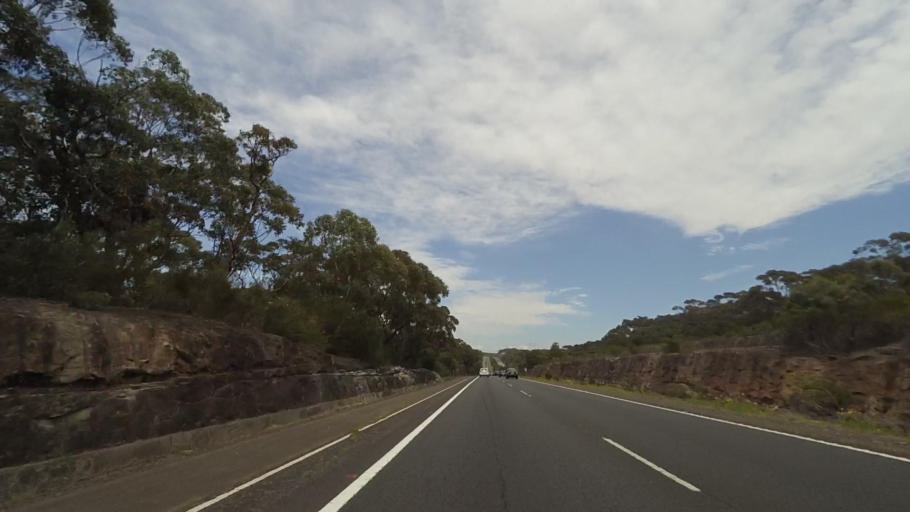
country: AU
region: New South Wales
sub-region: Wollongong
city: Helensburgh
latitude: -34.2126
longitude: 150.9595
